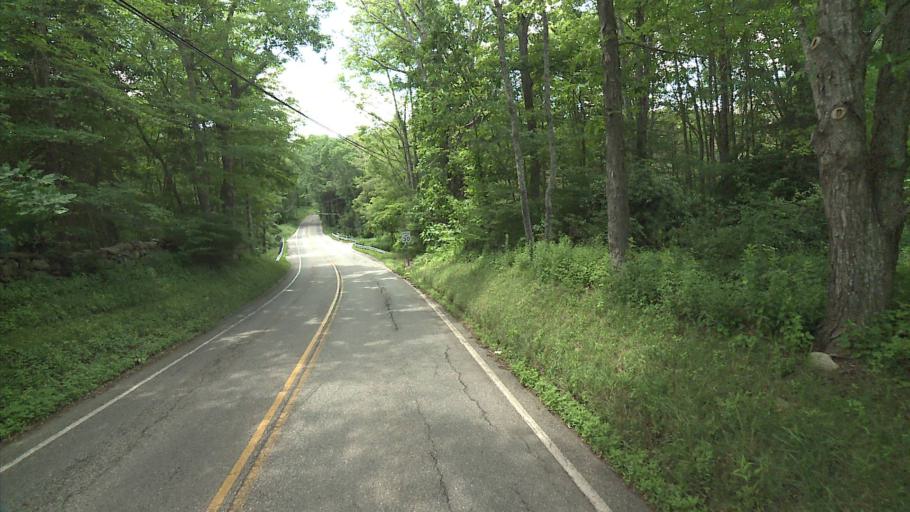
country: US
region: Connecticut
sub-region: New London County
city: Old Mystic
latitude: 41.4401
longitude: -71.9110
